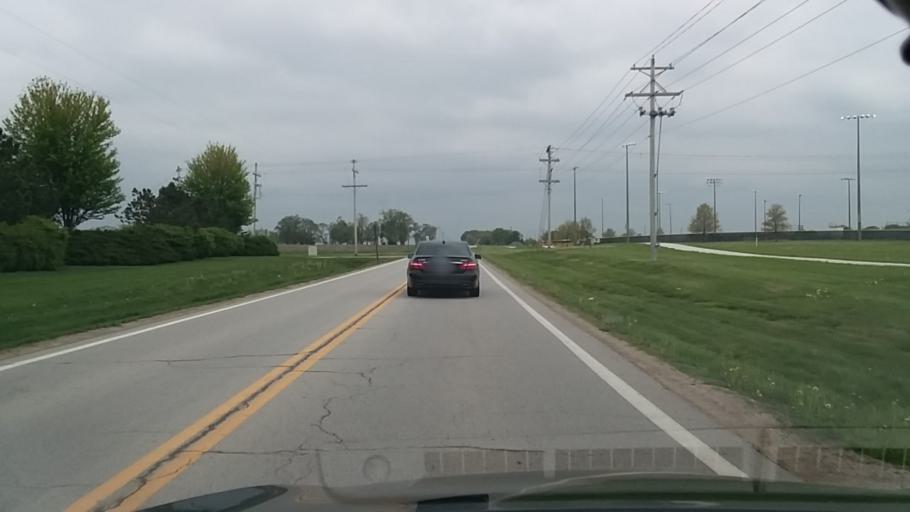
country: US
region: Kansas
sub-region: Douglas County
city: Eudora
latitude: 38.9214
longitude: -95.0935
